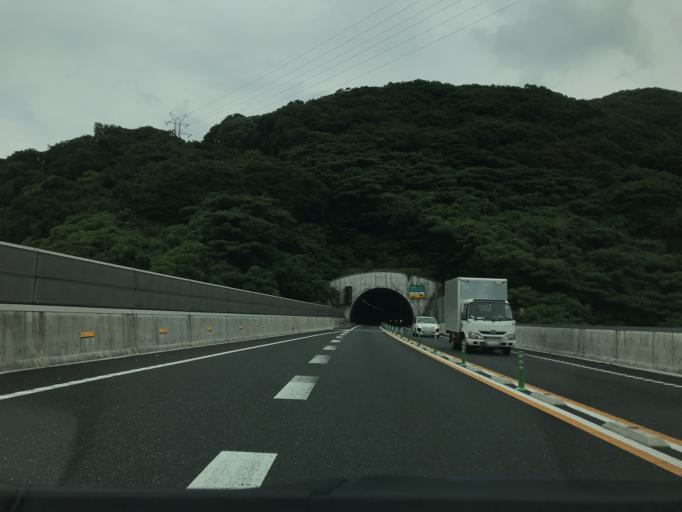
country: JP
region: Fukuoka
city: Kanda
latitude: 33.7918
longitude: 130.9691
